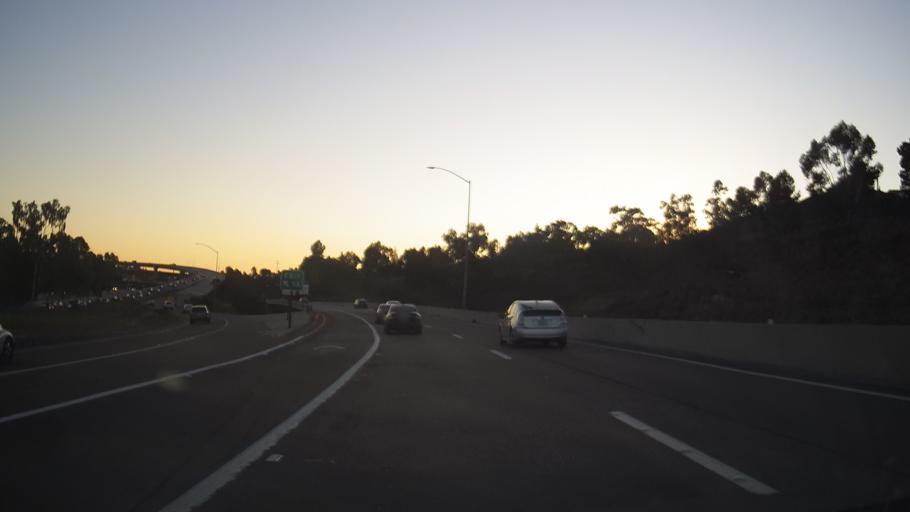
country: US
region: California
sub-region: San Diego County
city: Spring Valley
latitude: 32.7536
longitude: -117.0133
